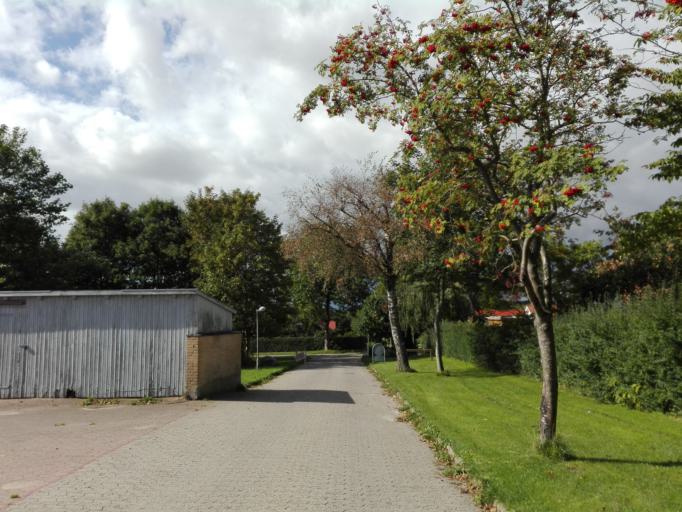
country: DK
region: Central Jutland
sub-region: Arhus Kommune
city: Beder
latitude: 56.0629
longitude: 10.2121
